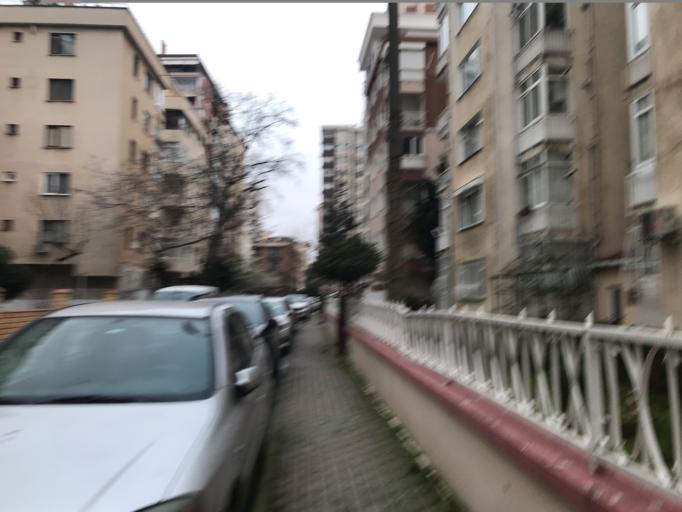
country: TR
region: Istanbul
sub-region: Atasehir
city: Atasehir
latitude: 40.9695
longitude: 29.0876
